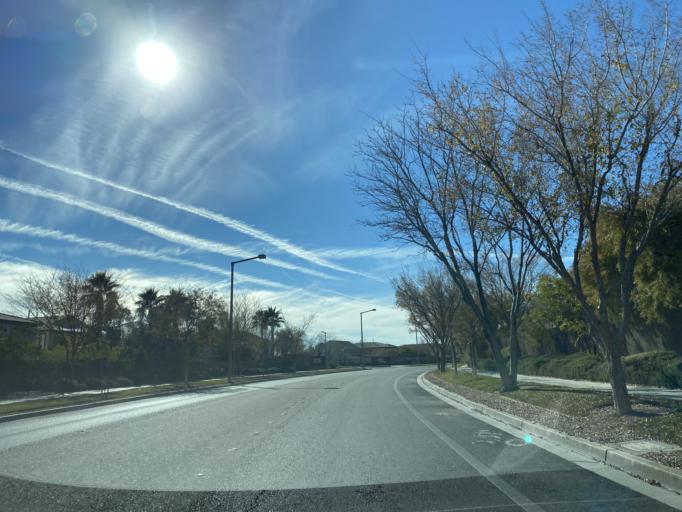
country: US
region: Nevada
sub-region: Clark County
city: Summerlin South
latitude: 36.1483
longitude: -115.3185
